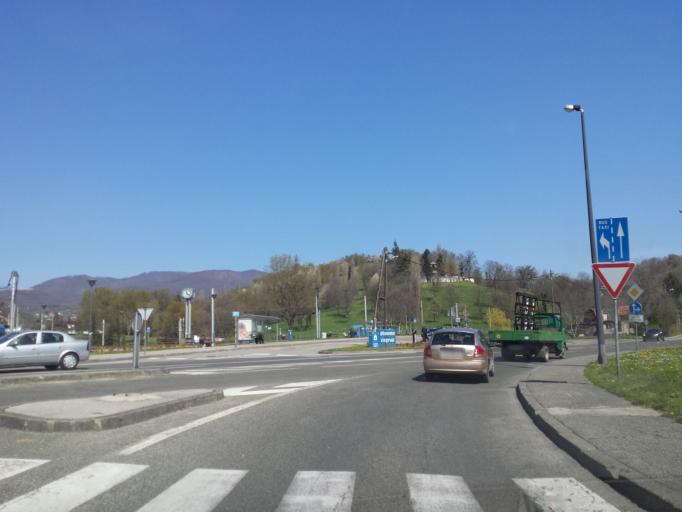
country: HR
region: Grad Zagreb
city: Zagreb
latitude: 45.8413
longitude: 15.9754
